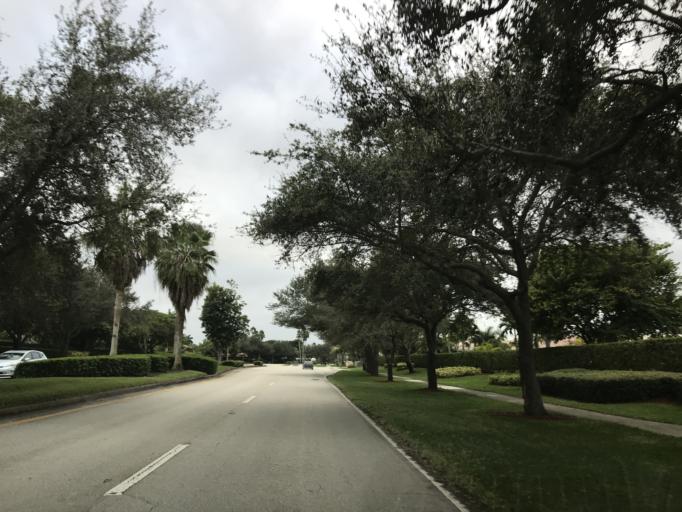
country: US
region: Florida
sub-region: Broward County
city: Coral Springs
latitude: 26.2990
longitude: -80.2733
